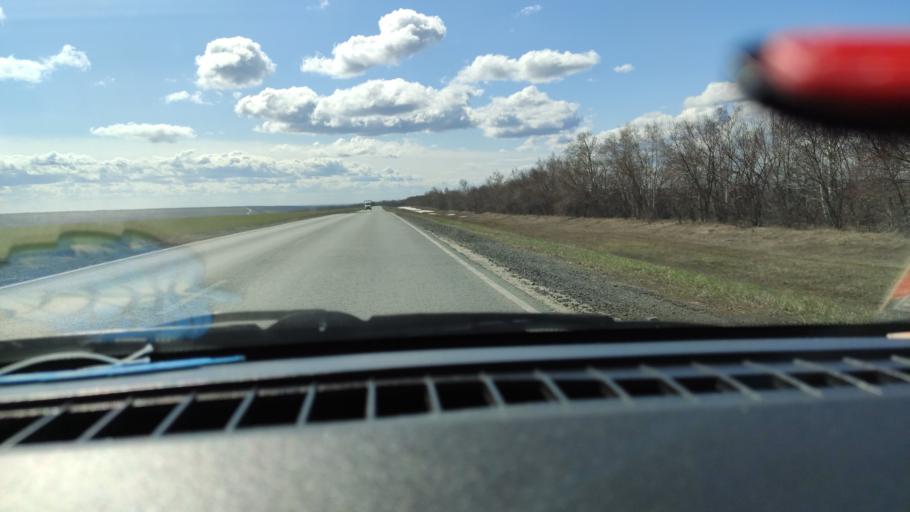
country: RU
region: Saratov
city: Dukhovnitskoye
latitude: 52.7675
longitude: 48.2371
